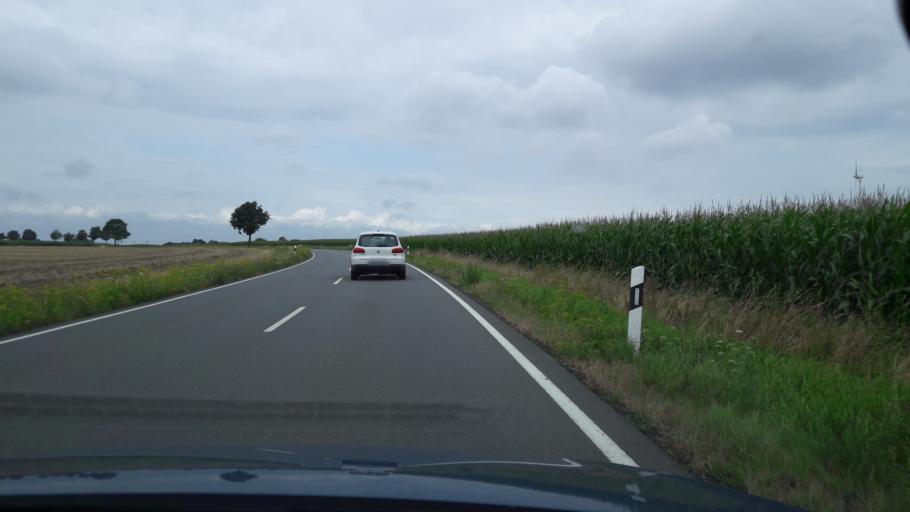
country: DE
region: North Rhine-Westphalia
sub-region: Regierungsbezirk Munster
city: Ennigerloh
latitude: 51.8619
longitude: 7.9735
